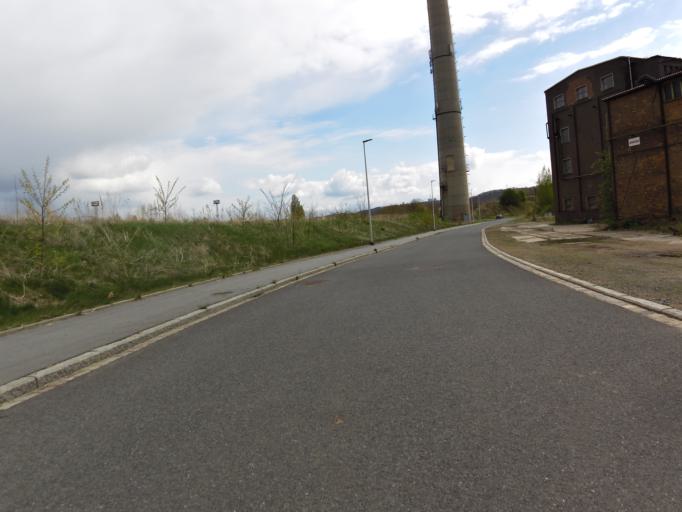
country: DE
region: Saxony
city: Coswig
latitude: 51.1118
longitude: 13.5837
